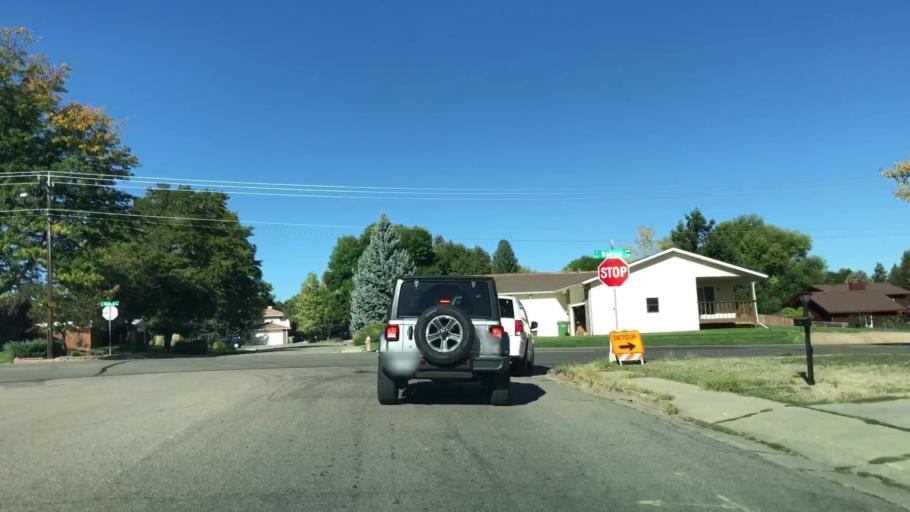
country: US
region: Colorado
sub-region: Larimer County
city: Loveland
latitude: 40.4143
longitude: -105.0583
